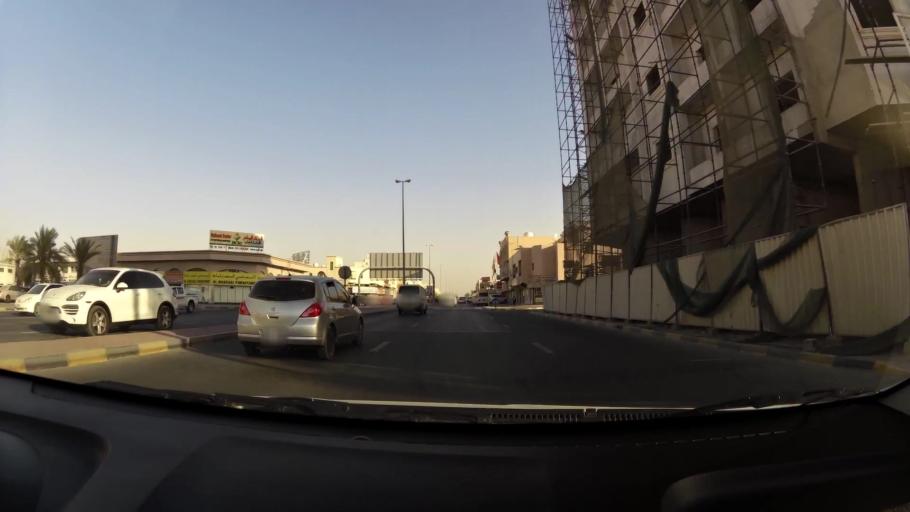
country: AE
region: Ajman
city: Ajman
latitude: 25.3978
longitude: 55.5047
